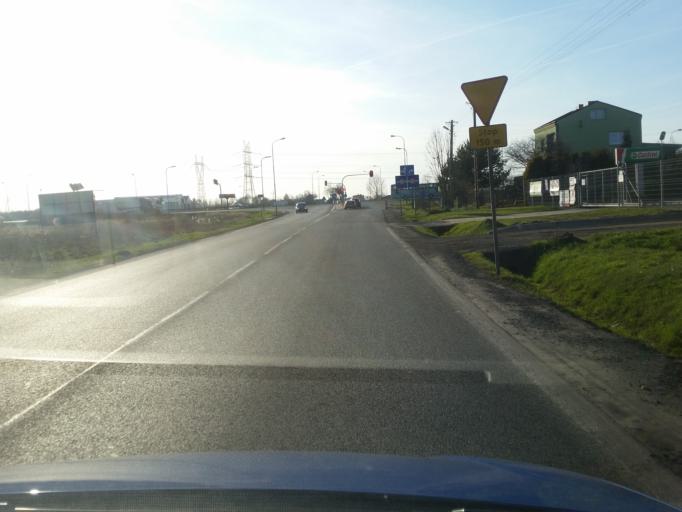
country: PL
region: Lodz Voivodeship
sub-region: Powiat radomszczanski
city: Radomsko
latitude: 51.0796
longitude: 19.3744
